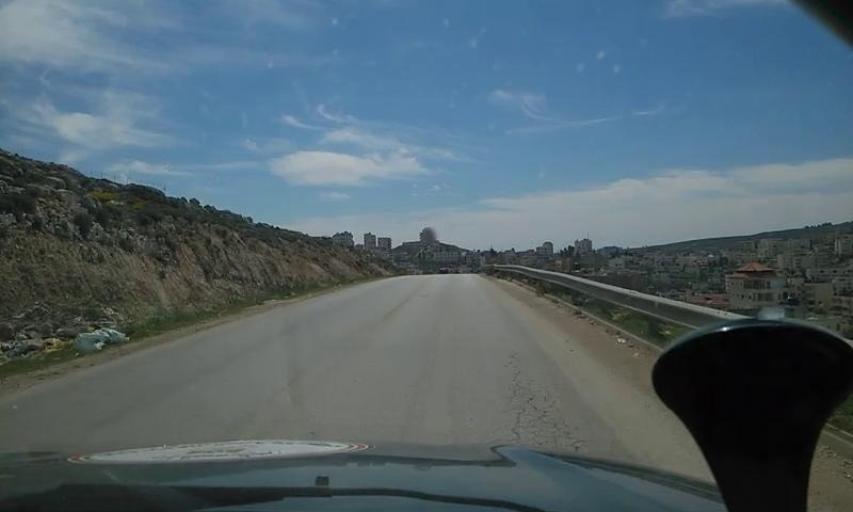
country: PS
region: West Bank
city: Al Judayrah
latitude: 31.8568
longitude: 35.2015
